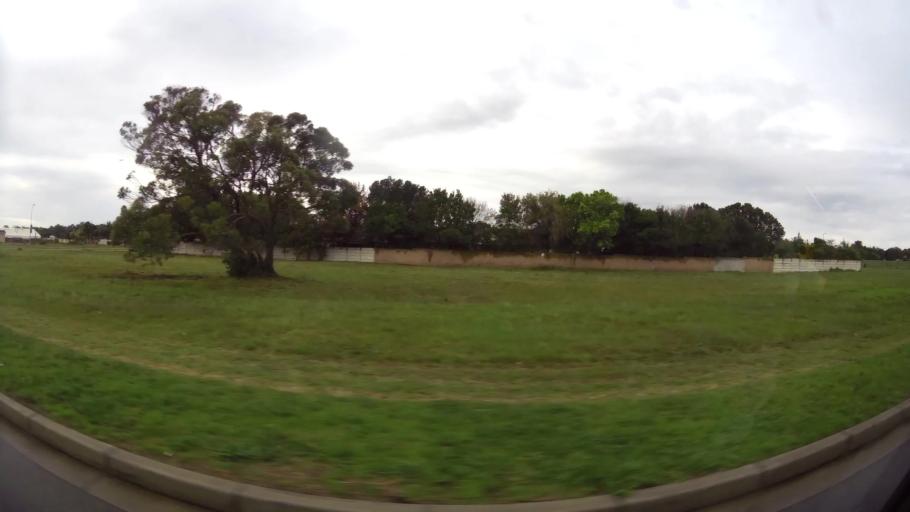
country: ZA
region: Eastern Cape
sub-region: Nelson Mandela Bay Metropolitan Municipality
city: Port Elizabeth
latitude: -33.9920
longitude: 25.5490
